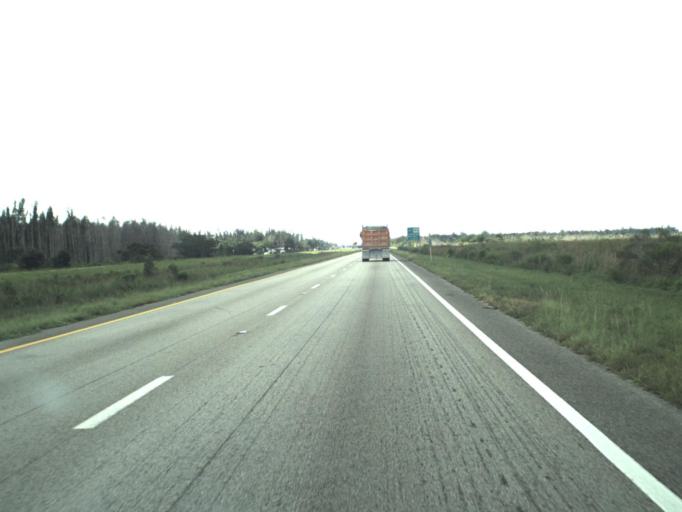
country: US
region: Florida
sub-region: Miami-Dade County
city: Palm Springs North
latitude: 25.9623
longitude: -80.4315
